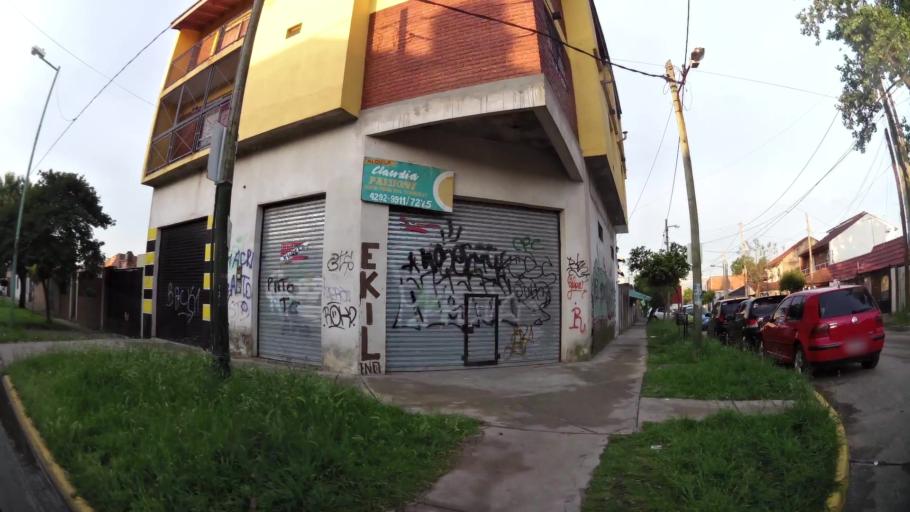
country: AR
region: Buenos Aires
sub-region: Partido de Almirante Brown
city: Adrogue
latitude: -34.7651
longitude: -58.3575
